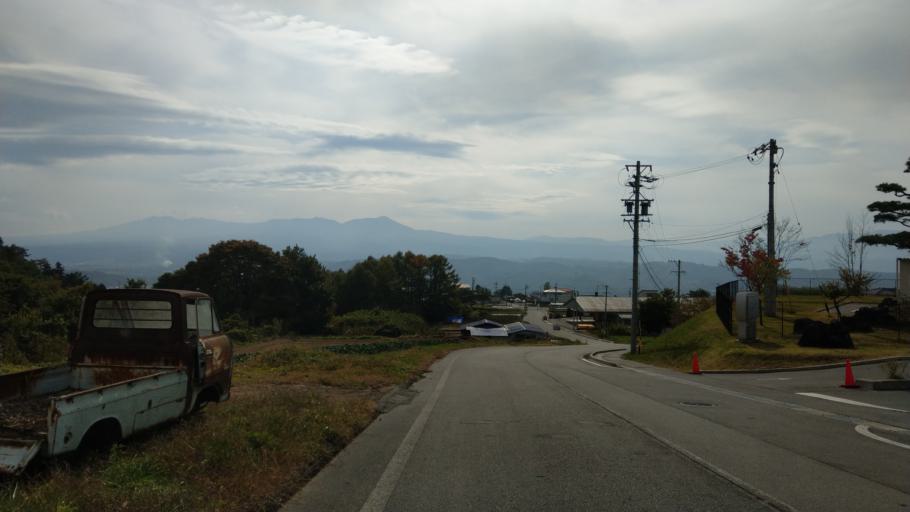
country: JP
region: Nagano
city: Komoro
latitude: 36.3488
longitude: 138.4368
